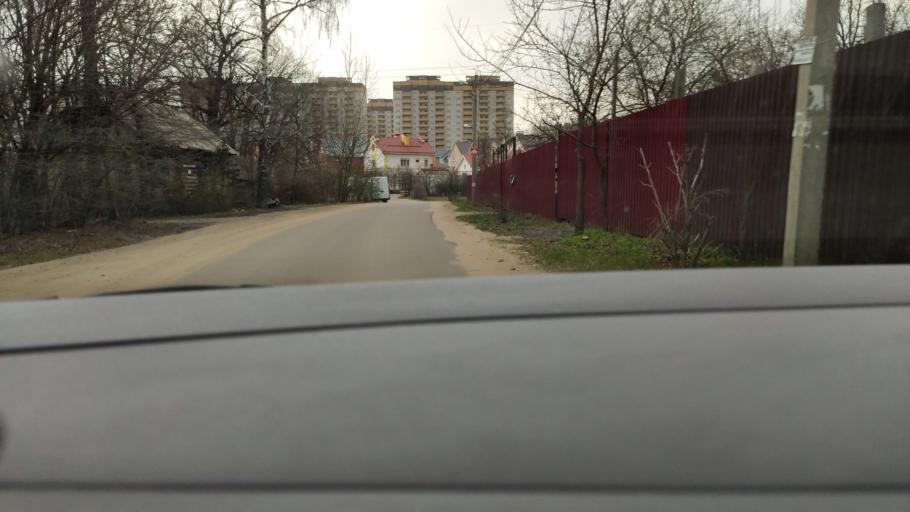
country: RU
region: Voronezj
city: Podgornoye
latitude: 51.7358
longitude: 39.1874
